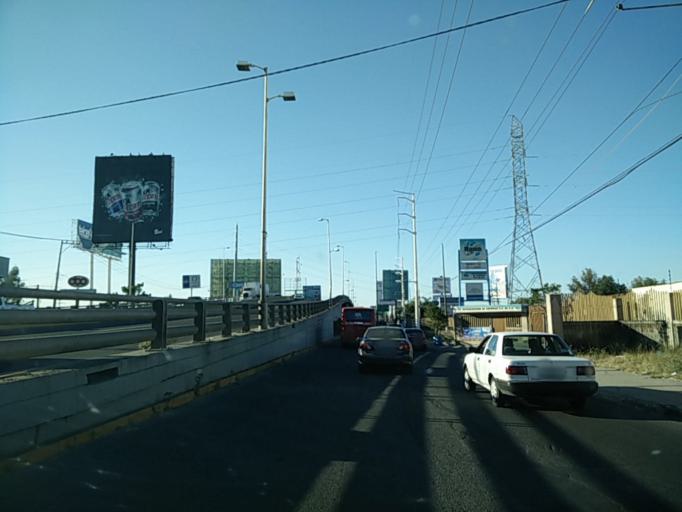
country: MX
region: Jalisco
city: Nuevo Mexico
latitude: 20.7007
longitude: -103.4591
